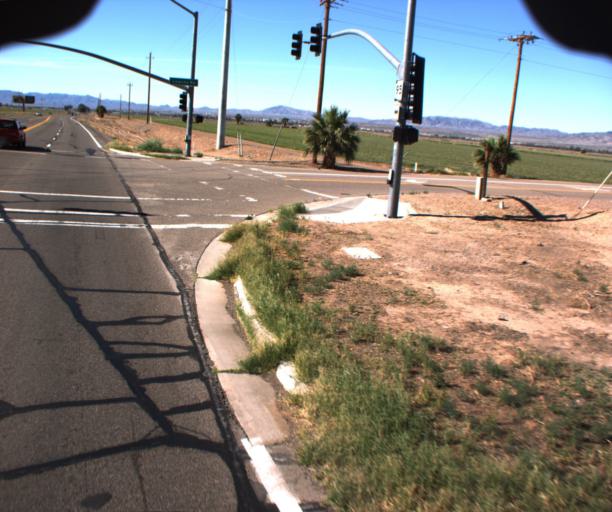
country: US
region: Arizona
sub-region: Mohave County
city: Willow Valley
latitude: 34.8954
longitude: -114.5980
